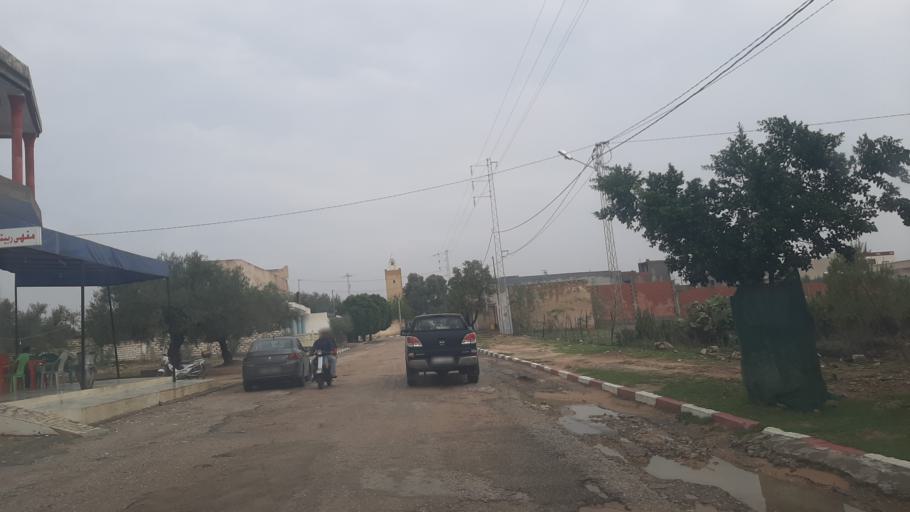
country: TN
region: Al Munastir
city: Sidi Bin Nur
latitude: 35.4787
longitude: 10.8736
